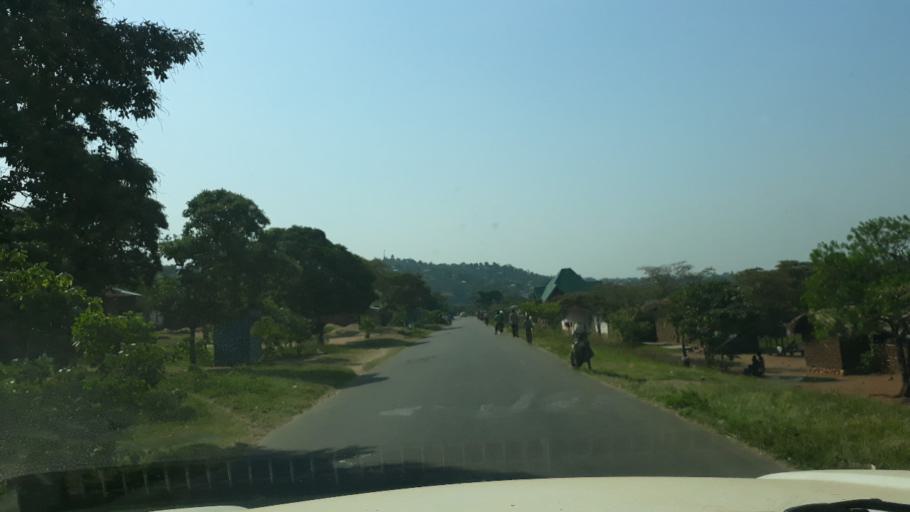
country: CD
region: South Kivu
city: Uvira
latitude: -3.2465
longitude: 29.1611
